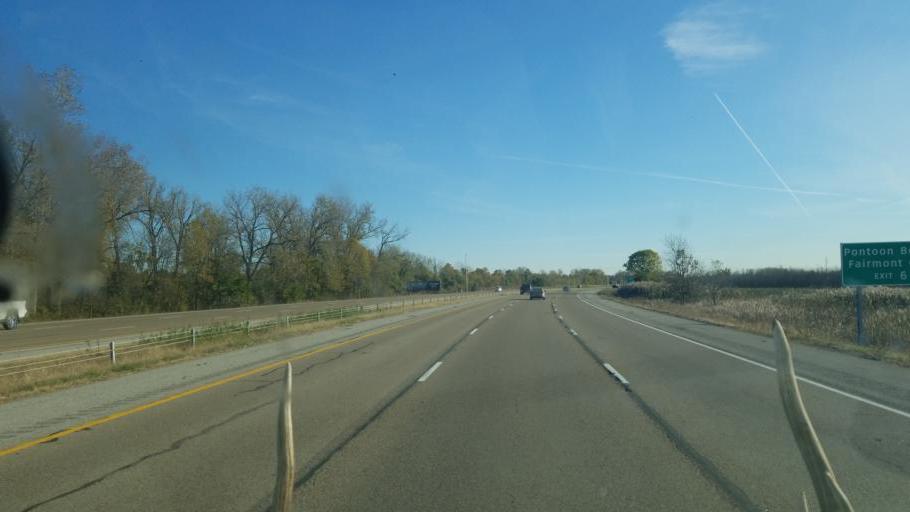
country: US
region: Illinois
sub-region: Saint Clair County
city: Fairmont City
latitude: 38.6610
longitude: -90.1050
